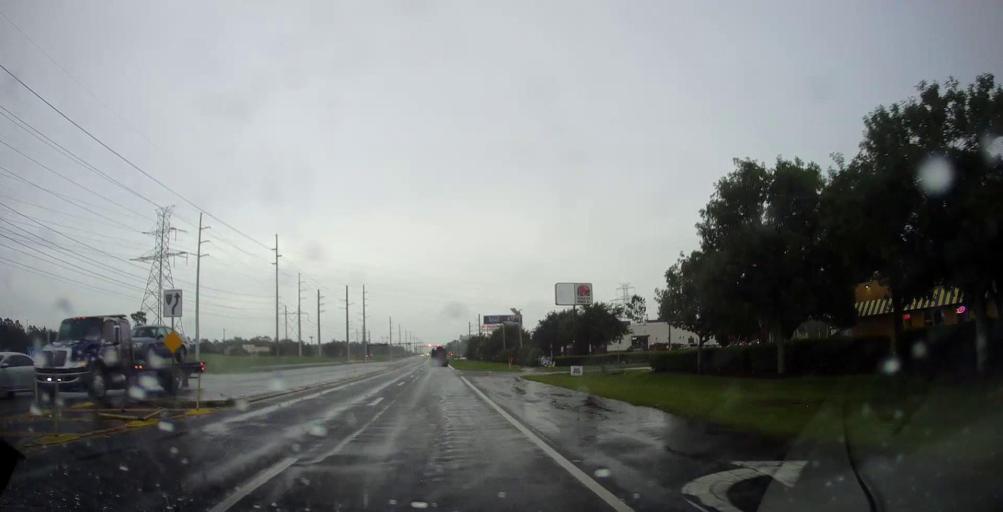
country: US
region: Florida
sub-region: Marion County
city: Silver Springs Shores
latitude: 29.1172
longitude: -82.0263
